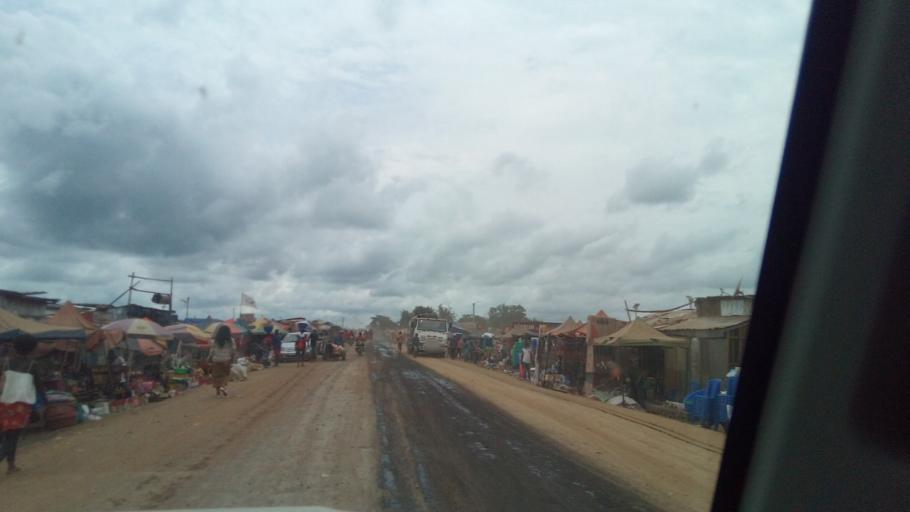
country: AO
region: Zaire
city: Mbanza Congo
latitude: -5.8348
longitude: 14.0756
